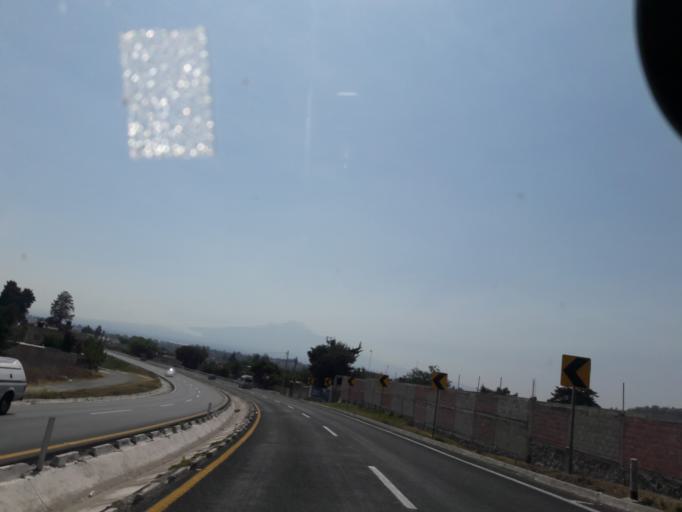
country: MX
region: Tlaxcala
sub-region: Totolac
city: Santiago Tepeticpac
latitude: 19.3363
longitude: -98.2253
